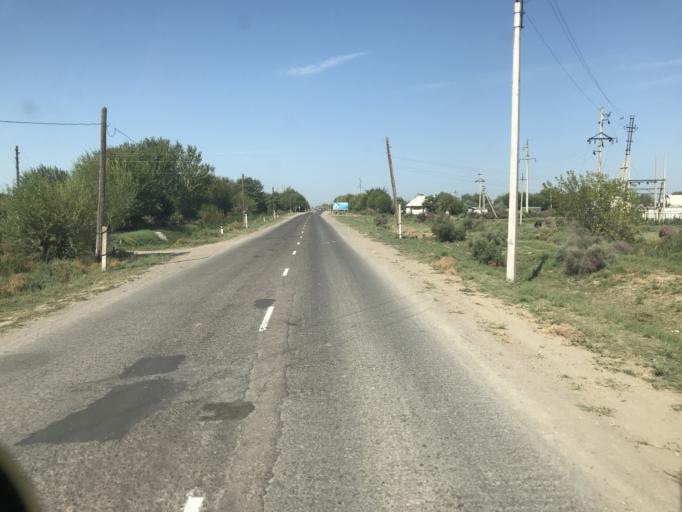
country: KZ
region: Ongtustik Qazaqstan
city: Myrzakent
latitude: 40.6850
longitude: 68.5937
